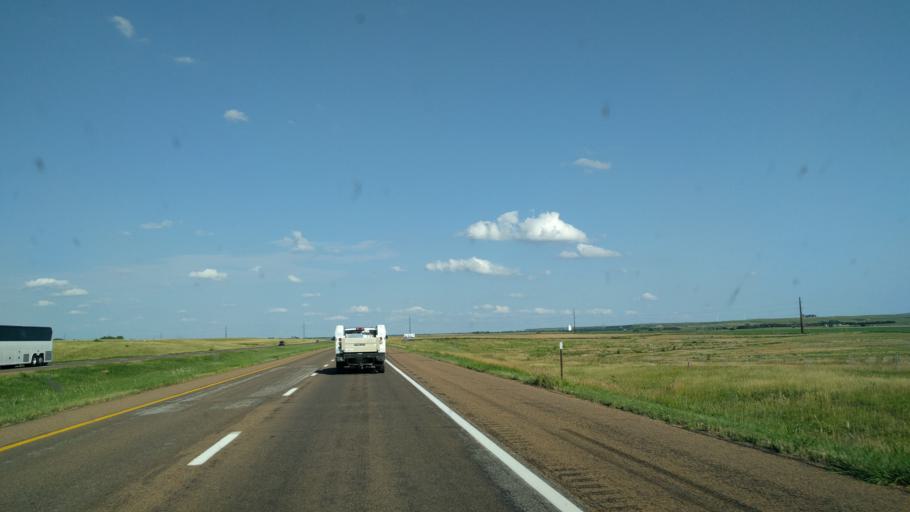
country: US
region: Kansas
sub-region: Ellis County
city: Ellis
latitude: 38.9349
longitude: -99.4713
